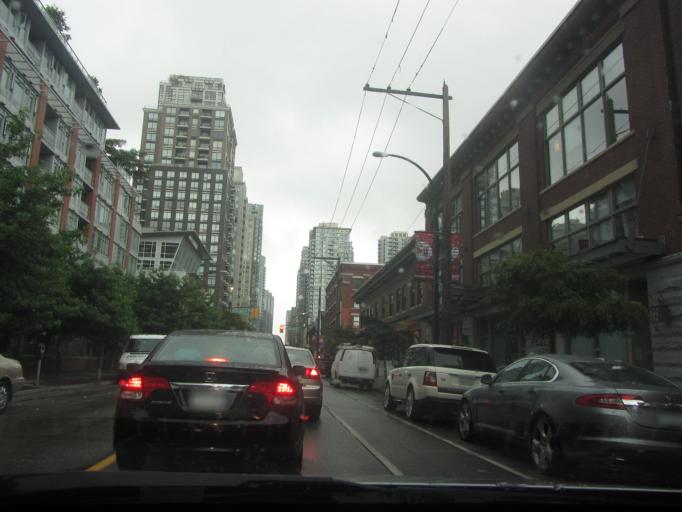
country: CA
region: British Columbia
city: West End
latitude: 49.2759
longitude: -123.1225
